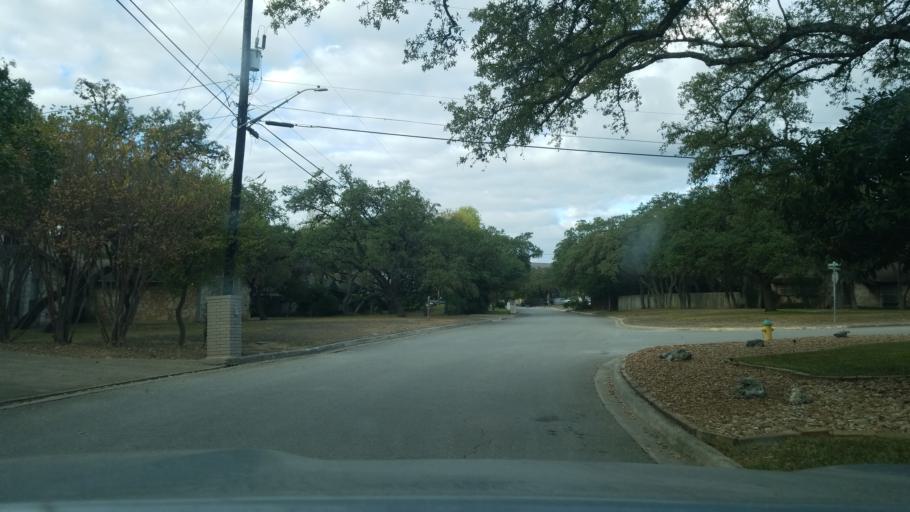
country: US
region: Texas
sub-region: Bexar County
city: Hollywood Park
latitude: 29.6057
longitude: -98.4812
